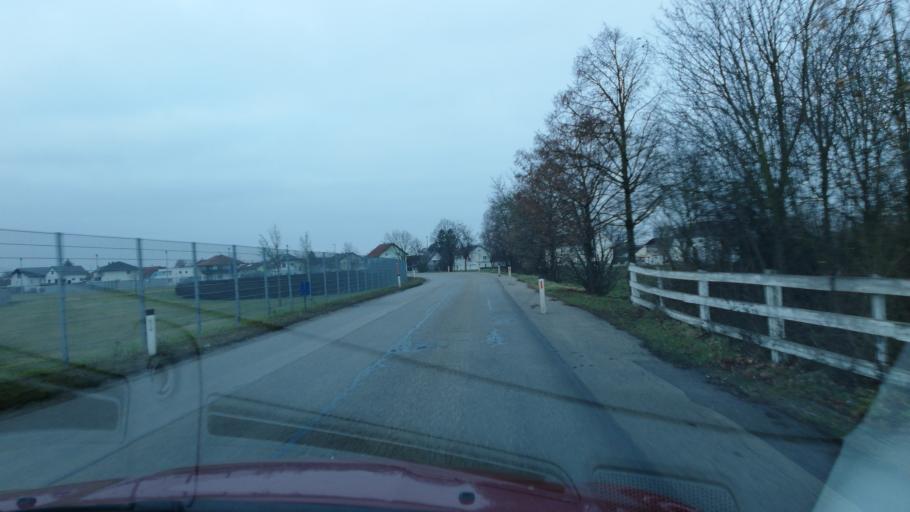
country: AT
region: Upper Austria
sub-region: Wels-Land
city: Marchtrenk
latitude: 48.1856
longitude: 14.0740
